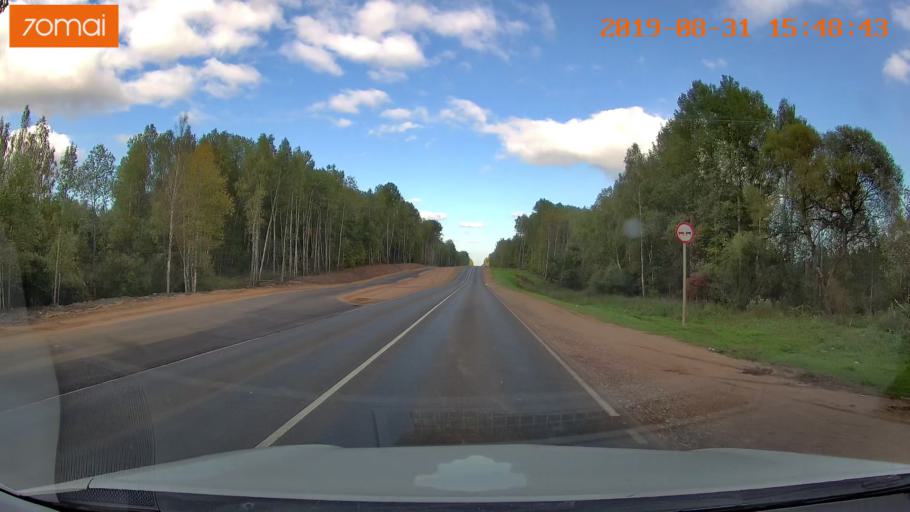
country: RU
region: Kaluga
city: Yukhnov
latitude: 54.6874
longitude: 35.0370
